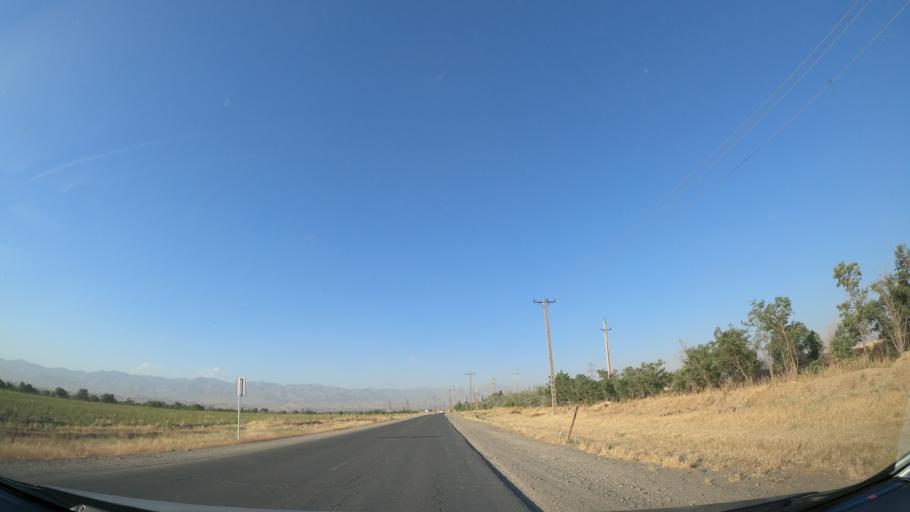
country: IR
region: Alborz
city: Hashtgerd
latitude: 35.9169
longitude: 50.7352
